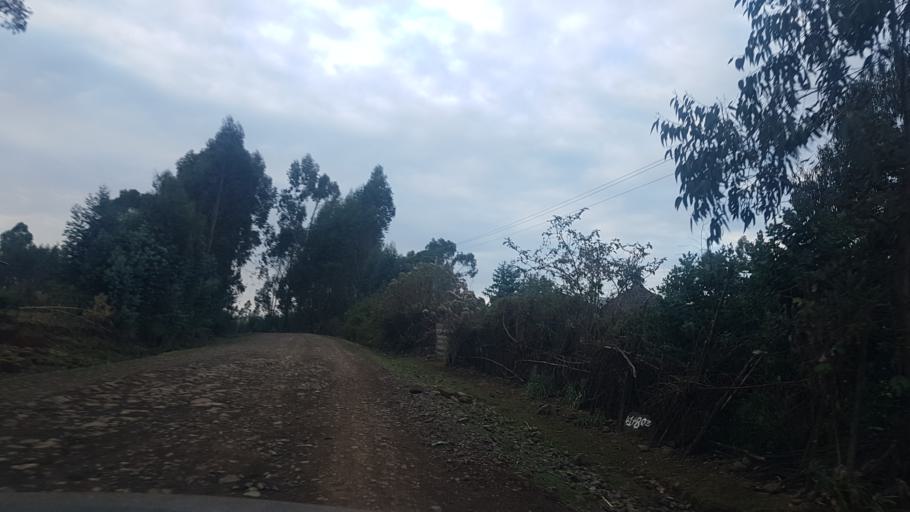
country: ET
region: Amhara
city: Finote Selam
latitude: 10.8109
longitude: 37.6530
